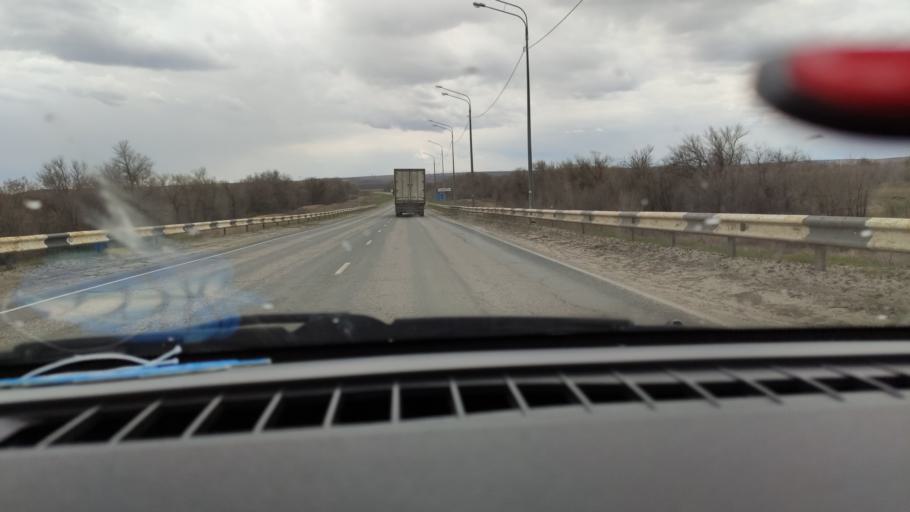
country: RU
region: Saratov
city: Sinodskoye
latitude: 51.9785
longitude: 46.6520
